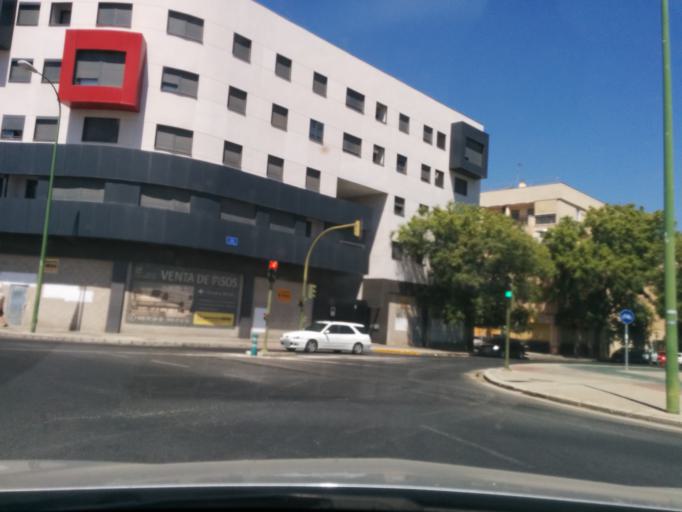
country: ES
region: Andalusia
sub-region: Provincia de Sevilla
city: Sevilla
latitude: 37.3632
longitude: -5.9740
